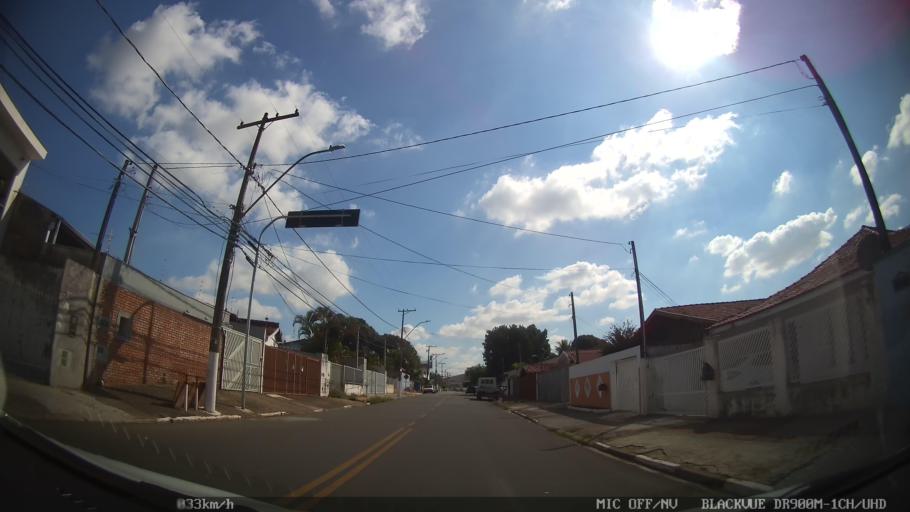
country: BR
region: Sao Paulo
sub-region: Hortolandia
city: Hortolandia
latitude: -22.8744
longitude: -47.2221
